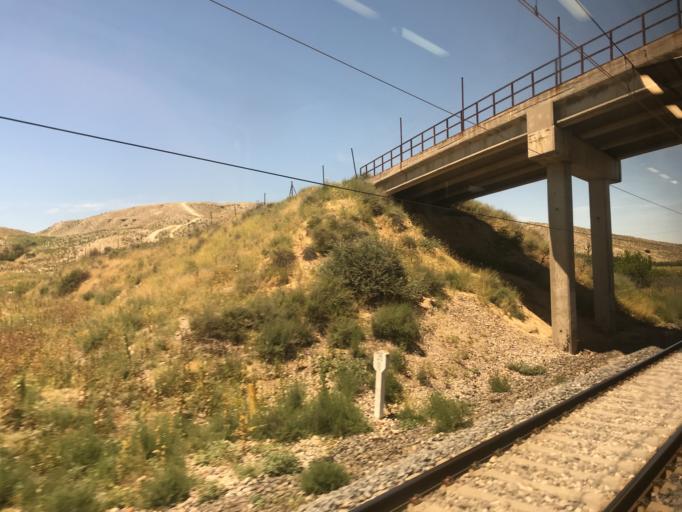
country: ES
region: Madrid
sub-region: Provincia de Madrid
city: Ciempozuelos
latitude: 40.1379
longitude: -3.6122
